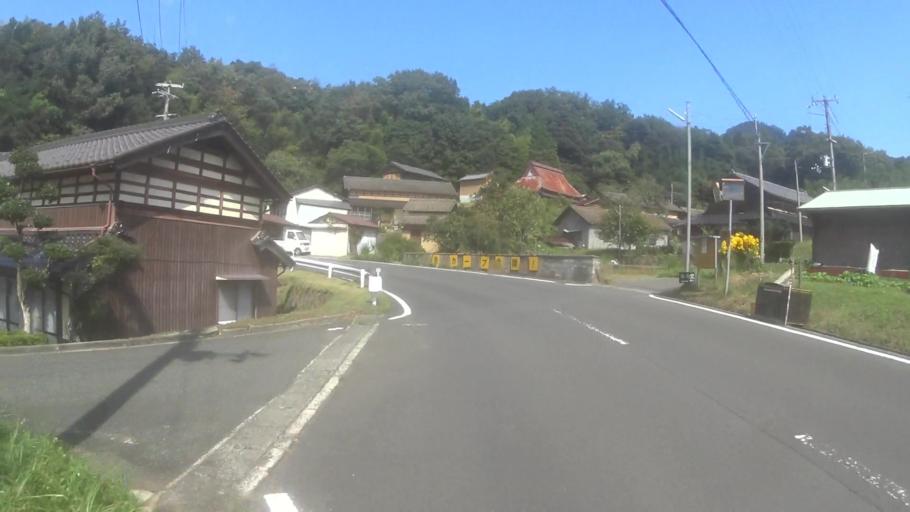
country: JP
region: Kyoto
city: Miyazu
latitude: 35.6187
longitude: 135.1315
